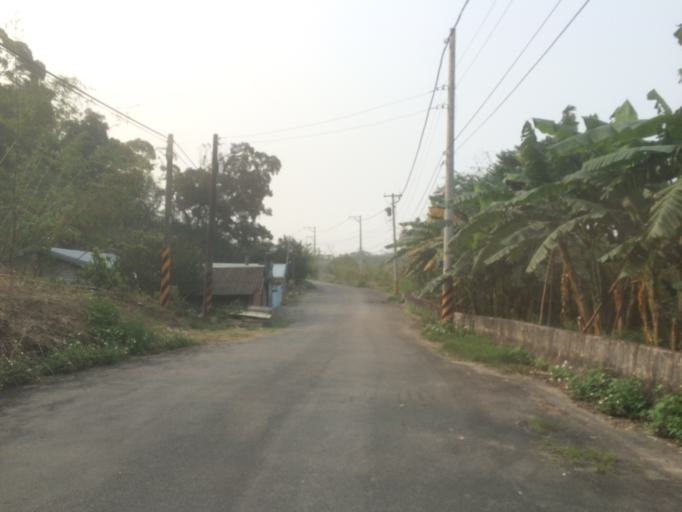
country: TW
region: Taiwan
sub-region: Hsinchu
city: Hsinchu
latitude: 24.7643
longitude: 120.9744
